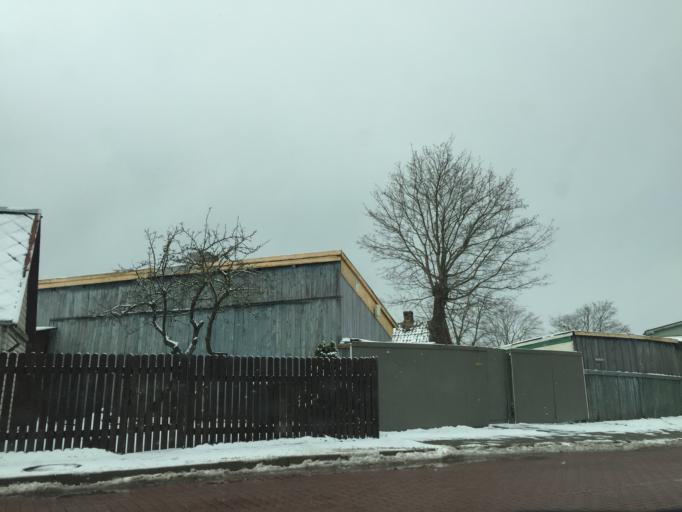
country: LV
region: Ventspils
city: Ventspils
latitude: 57.3933
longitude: 21.5509
